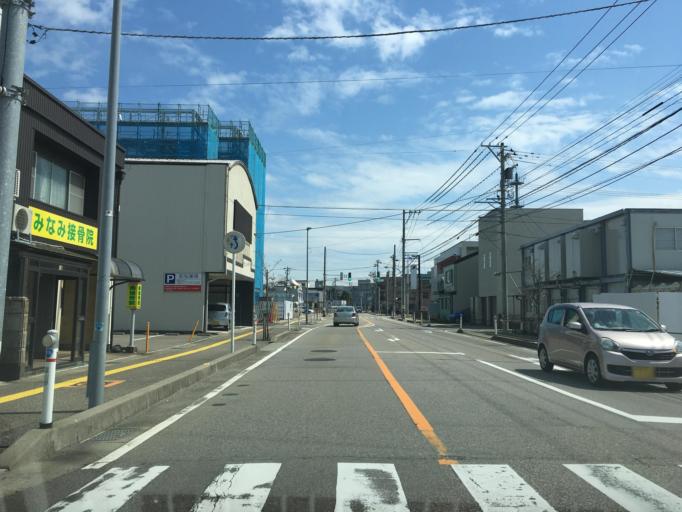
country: JP
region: Toyama
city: Nishishinminato
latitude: 36.7826
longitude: 137.0780
